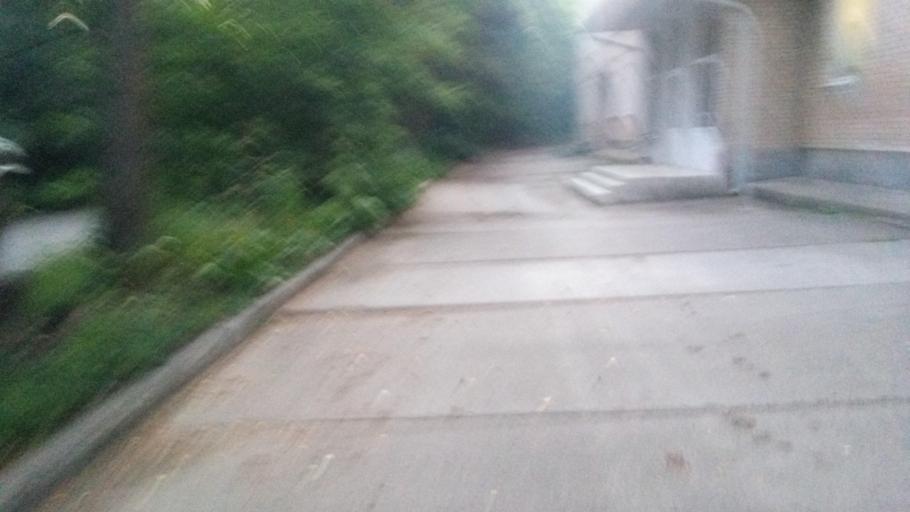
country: RU
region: Chelyabinsk
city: Turgoyak
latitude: 55.1527
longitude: 60.1613
